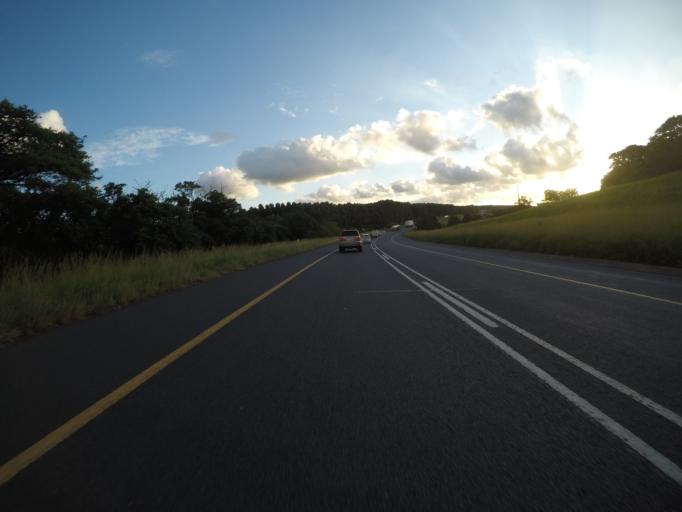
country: ZA
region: KwaZulu-Natal
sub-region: uThungulu District Municipality
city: Richards Bay
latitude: -28.6912
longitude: 32.0370
